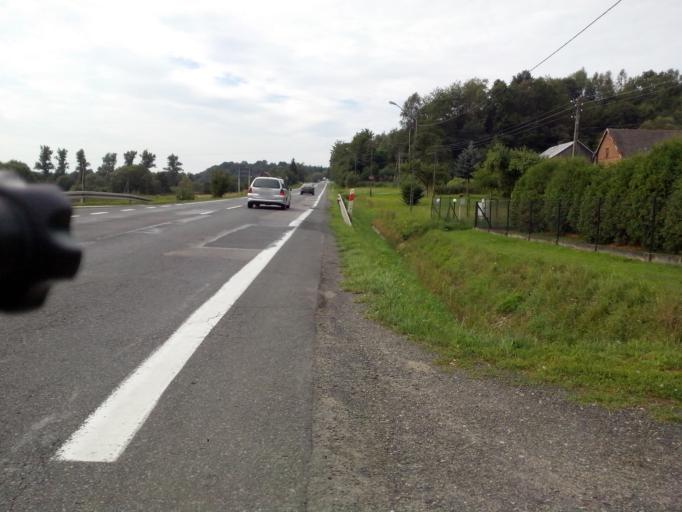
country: PL
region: Subcarpathian Voivodeship
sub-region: Powiat brzozowski
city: Domaradz
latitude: 49.7774
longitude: 21.9447
